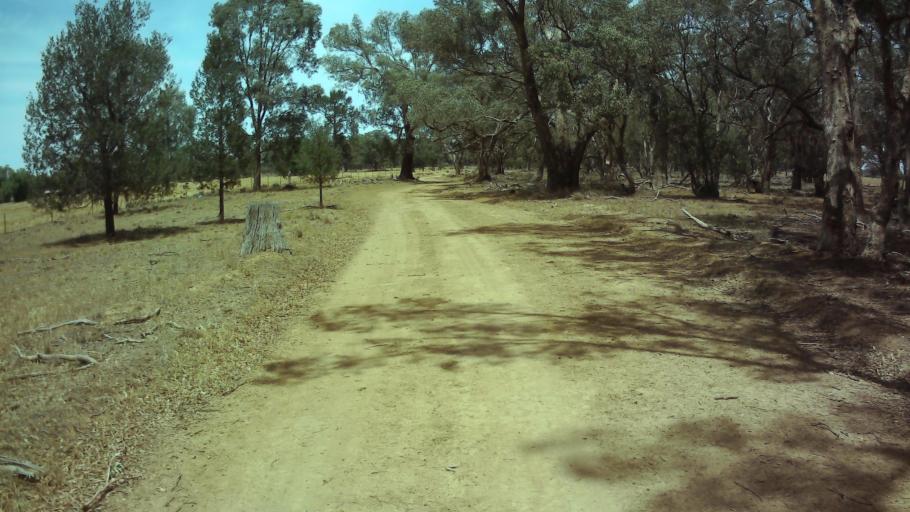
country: AU
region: New South Wales
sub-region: Weddin
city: Grenfell
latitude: -34.0325
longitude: 147.9311
